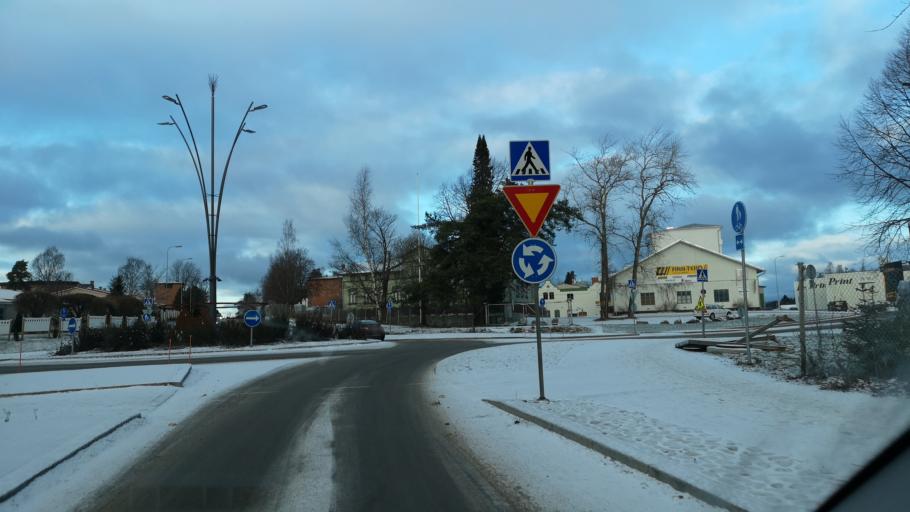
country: FI
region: Ostrobothnia
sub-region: Vaasa
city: Vaasa
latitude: 63.1157
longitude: 21.6184
